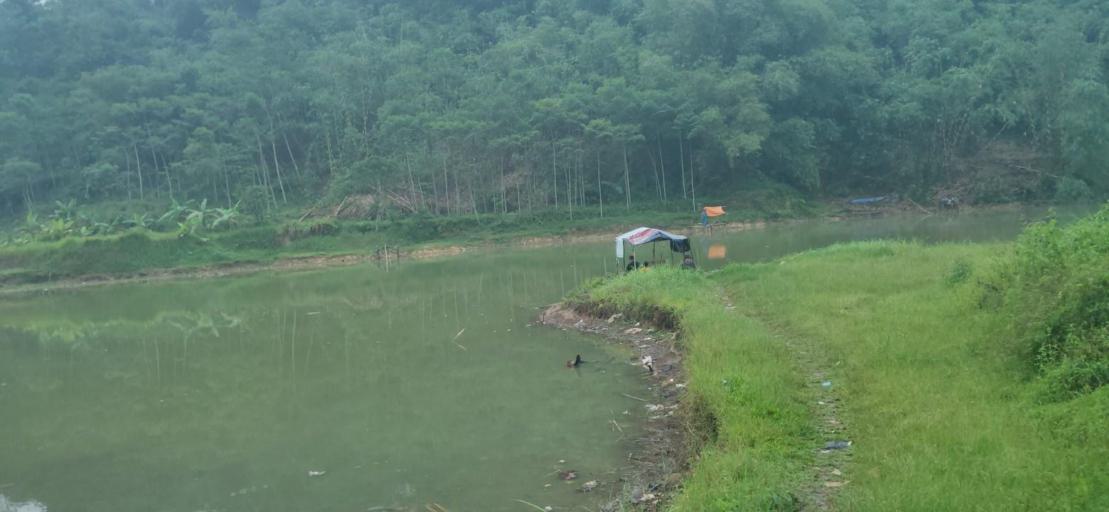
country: ID
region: West Java
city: Cipatat
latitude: -6.6334
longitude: 106.5231
